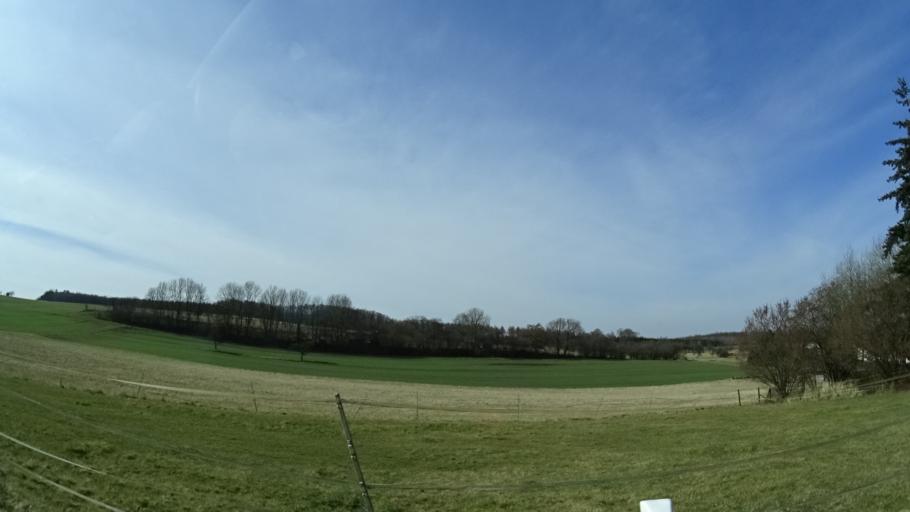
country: DE
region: Hesse
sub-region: Regierungsbezirk Giessen
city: Grunberg
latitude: 50.6295
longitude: 9.0656
